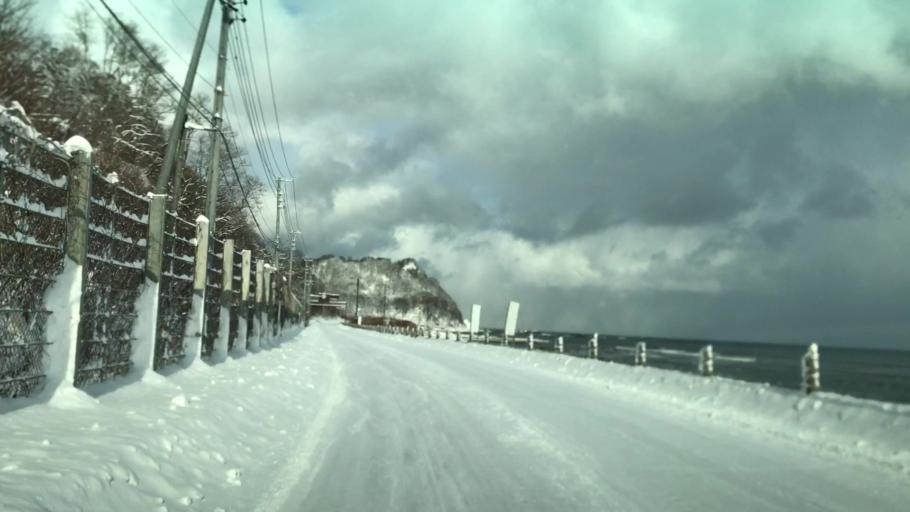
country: JP
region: Hokkaido
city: Yoichi
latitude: 43.2882
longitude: 140.6334
